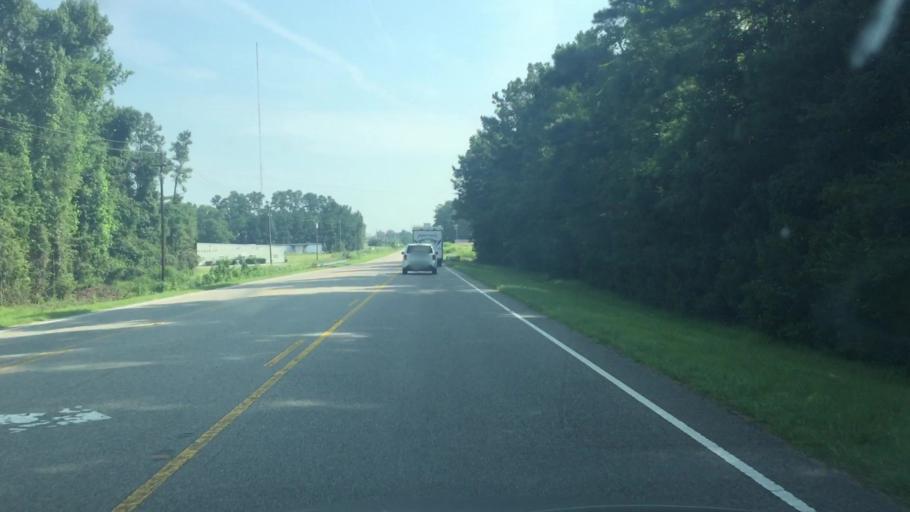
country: US
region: North Carolina
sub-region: Columbus County
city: Tabor City
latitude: 34.1480
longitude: -78.8624
